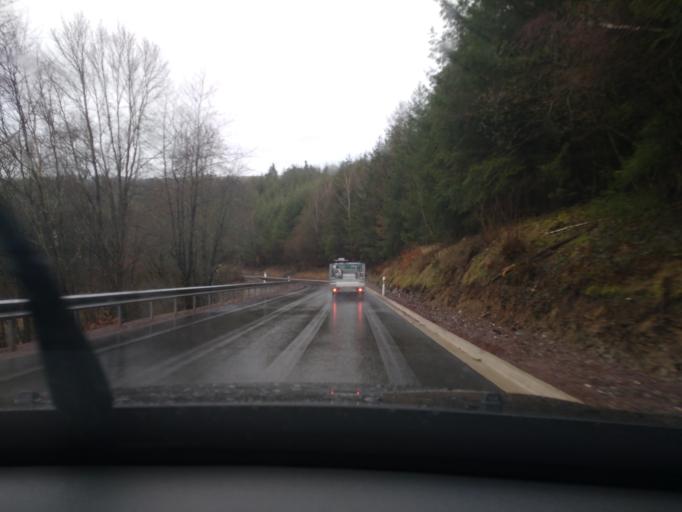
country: DE
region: Rheinland-Pfalz
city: Hinzenburg
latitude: 49.6752
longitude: 6.7296
